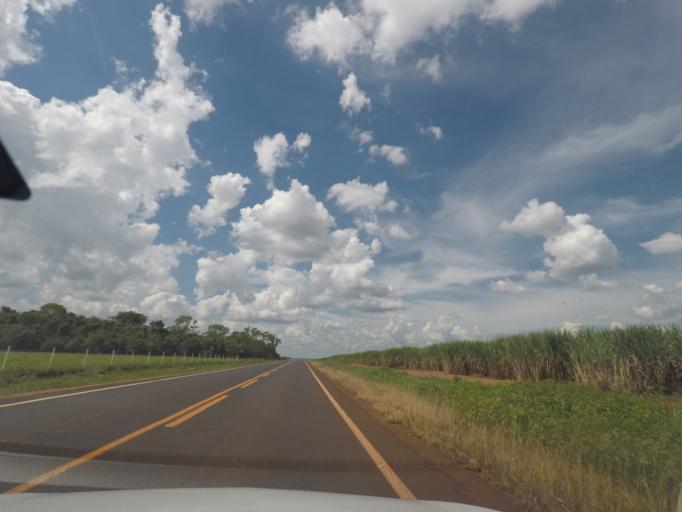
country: BR
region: Minas Gerais
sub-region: Conceicao Das Alagoas
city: Conceicao das Alagoas
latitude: -19.8497
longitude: -48.5975
